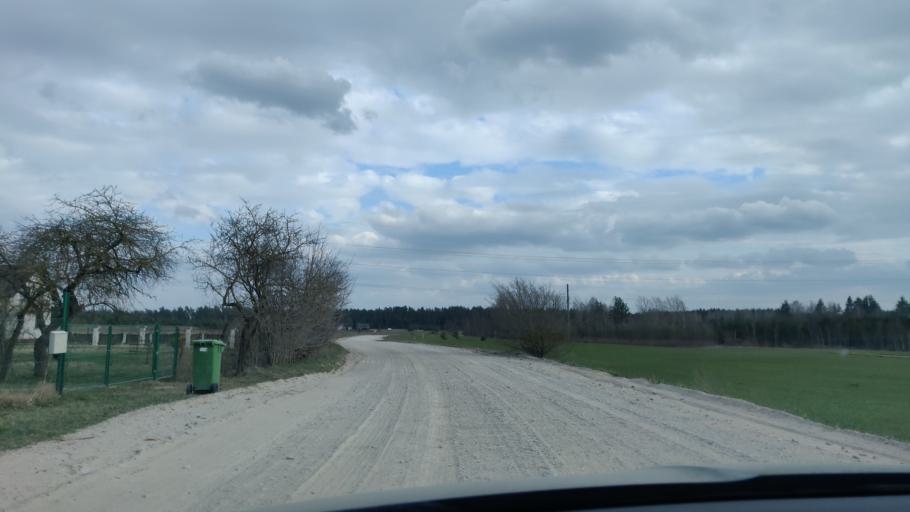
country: LT
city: Lentvaris
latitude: 54.6094
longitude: 25.0716
